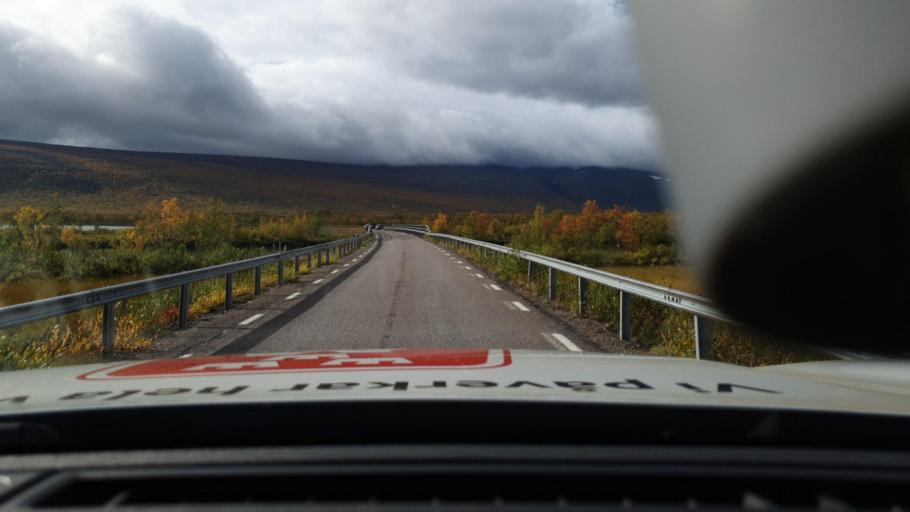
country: SE
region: Norrbotten
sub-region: Kiruna Kommun
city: Kiruna
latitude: 67.8615
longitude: 19.0308
